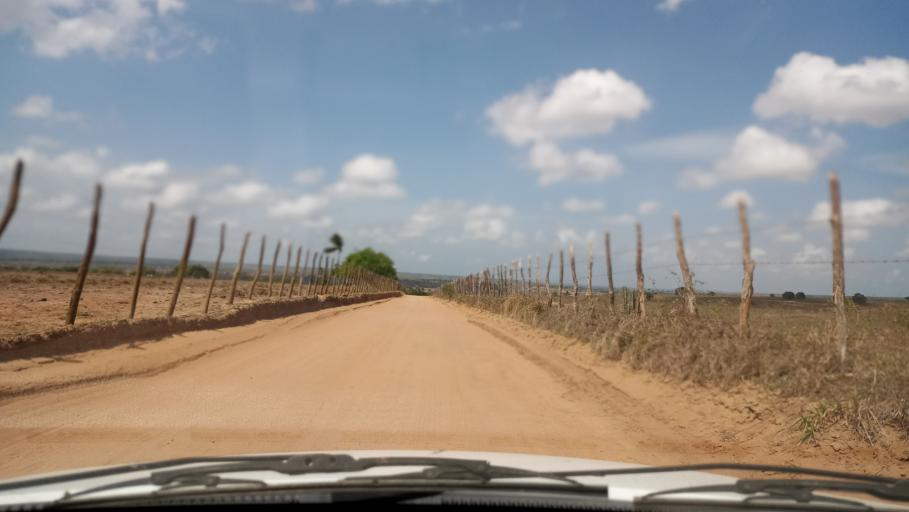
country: BR
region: Rio Grande do Norte
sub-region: Pedro Velho
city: Pedro Velho
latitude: -6.3484
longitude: -35.3311
